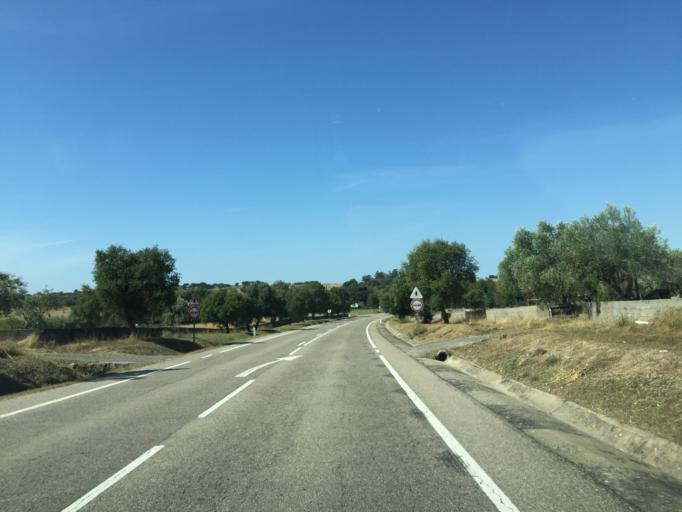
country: PT
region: Portalegre
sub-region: Castelo de Vide
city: Castelo de Vide
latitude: 39.4283
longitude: -7.4921
